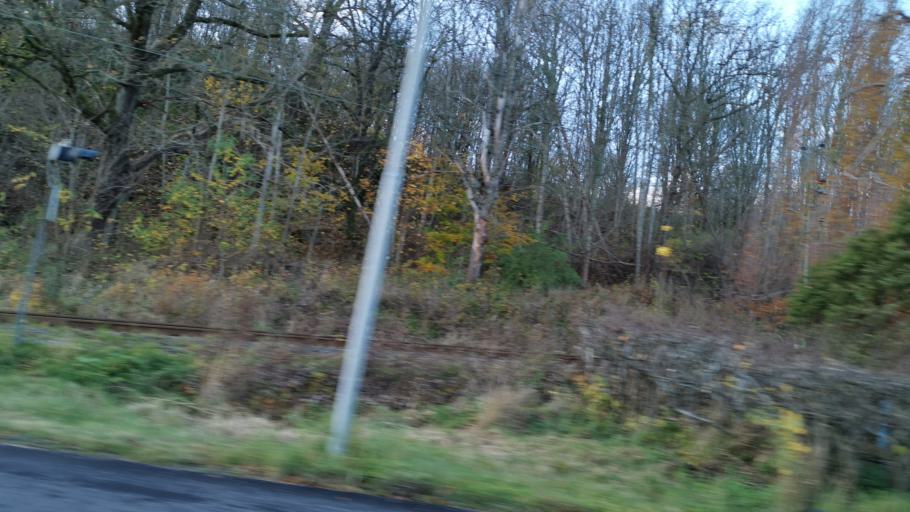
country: SE
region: Vaestra Goetaland
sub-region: Munkedals Kommun
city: Munkedal
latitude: 58.4725
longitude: 11.6737
